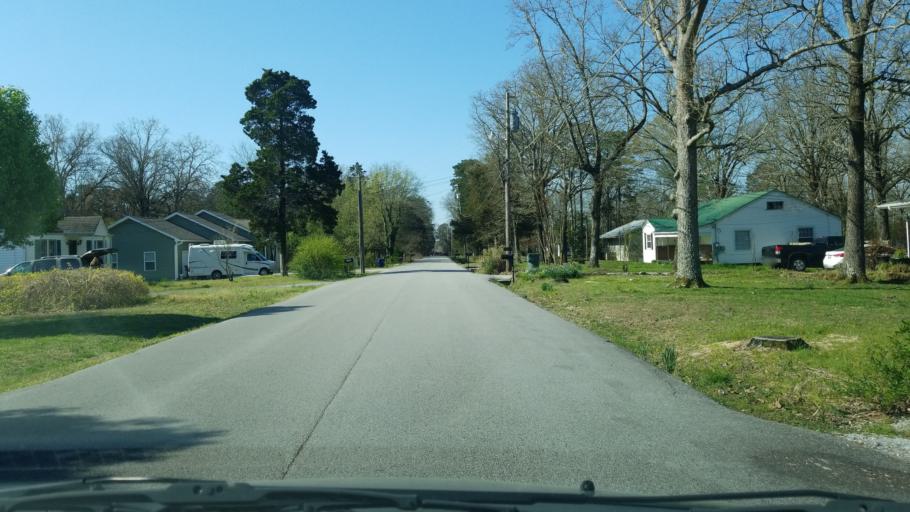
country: US
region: Tennessee
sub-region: Hamilton County
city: Harrison
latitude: 35.0639
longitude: -85.1438
